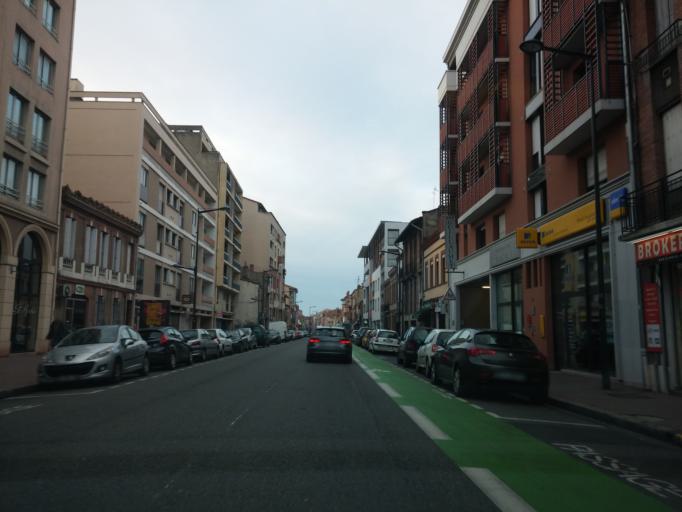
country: FR
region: Midi-Pyrenees
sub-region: Departement de la Haute-Garonne
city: Toulouse
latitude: 43.5872
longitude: 1.4468
